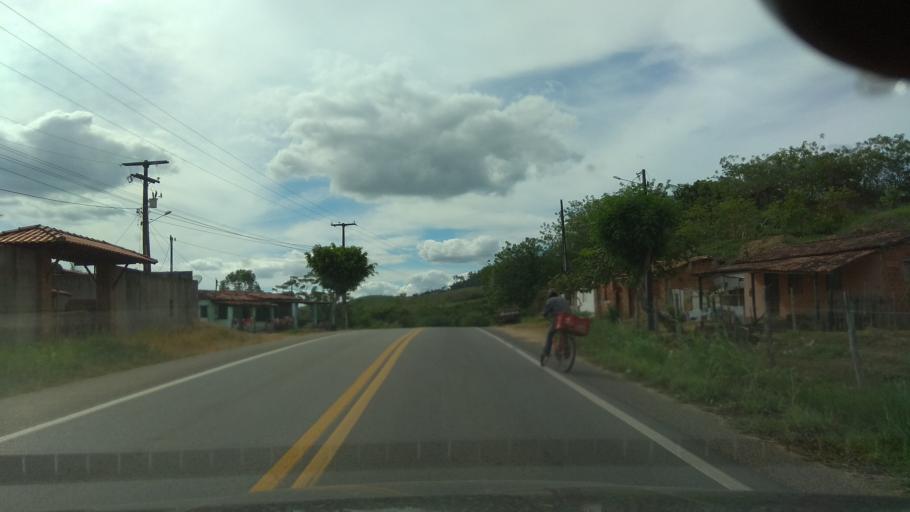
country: BR
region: Bahia
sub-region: Ipiau
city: Ipiau
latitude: -14.1128
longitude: -39.7729
